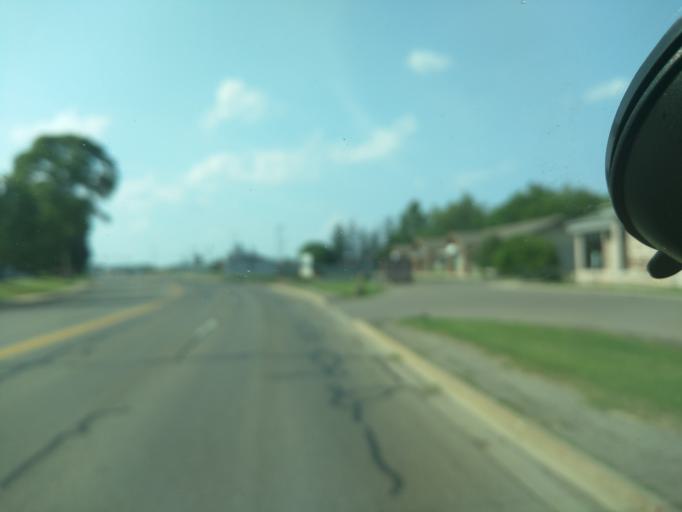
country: US
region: Michigan
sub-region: Jackson County
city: Jackson
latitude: 42.2601
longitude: -84.4477
